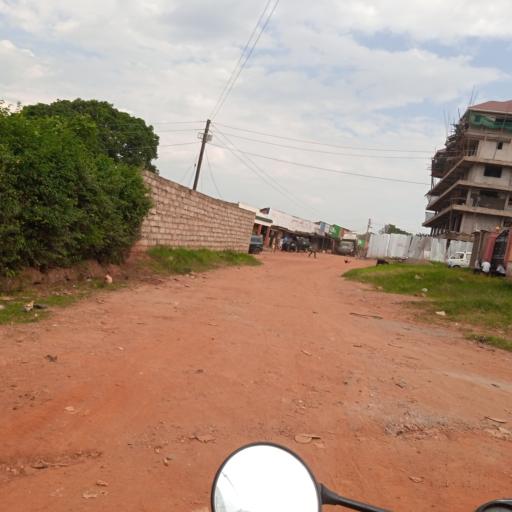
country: UG
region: Eastern Region
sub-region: Mbale District
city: Mbale
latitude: 1.0793
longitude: 34.1796
